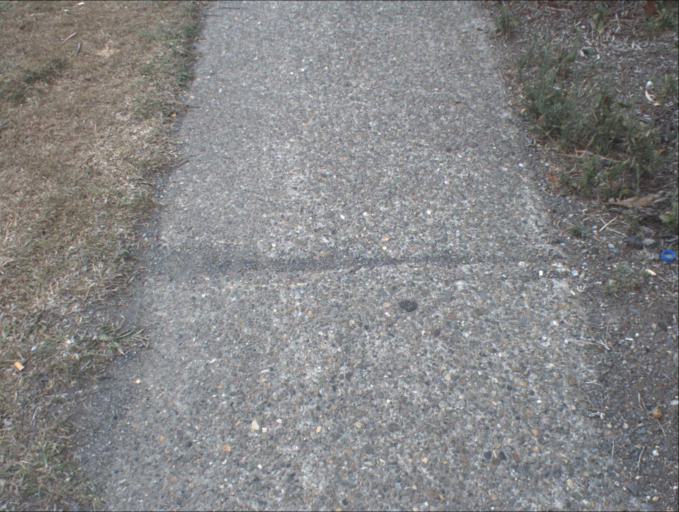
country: AU
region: Queensland
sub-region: Logan
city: Beenleigh
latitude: -27.7195
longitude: 153.2039
